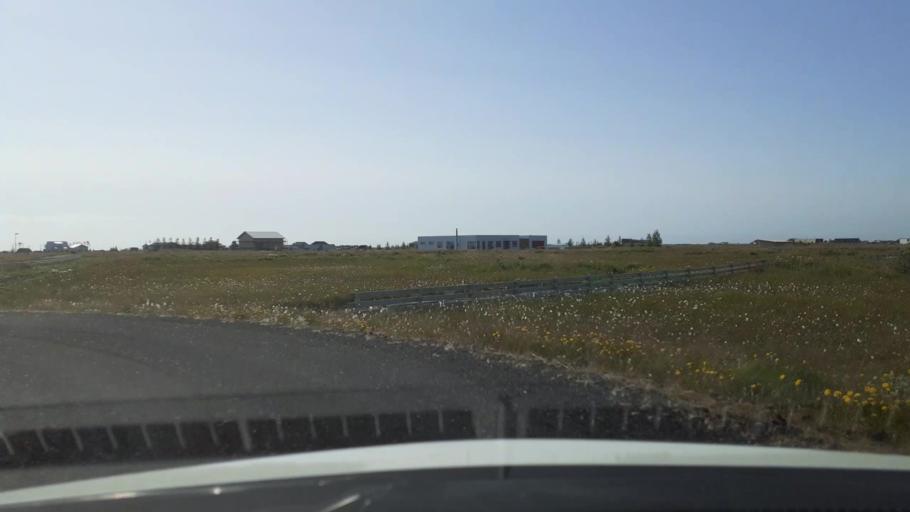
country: IS
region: South
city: Selfoss
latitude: 63.9000
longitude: -21.0807
